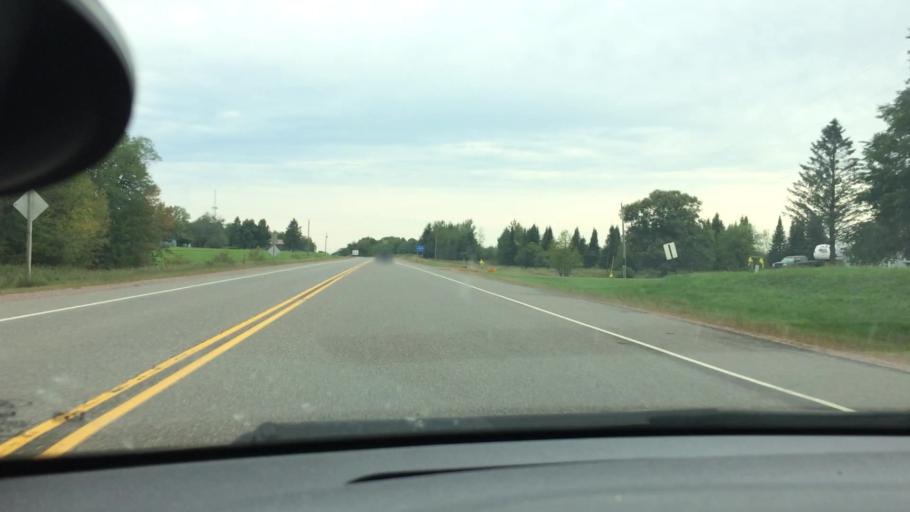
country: US
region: Wisconsin
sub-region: Clark County
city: Neillsville
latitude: 44.5605
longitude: -90.6463
